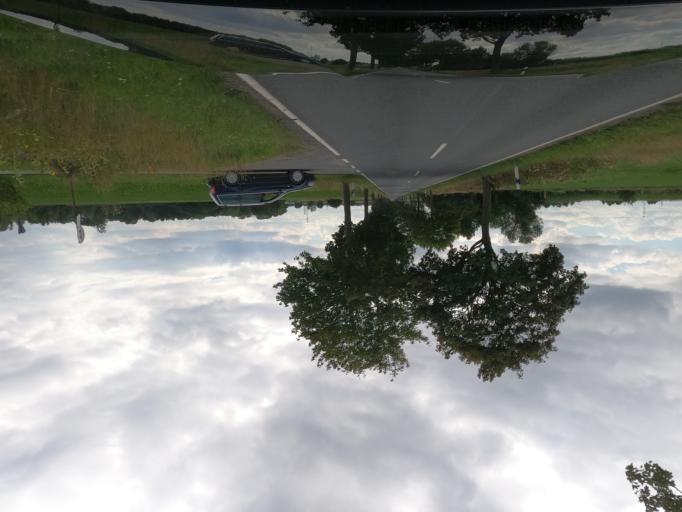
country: DE
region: Lower Saxony
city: Lehrte
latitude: 52.3388
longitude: 10.0280
